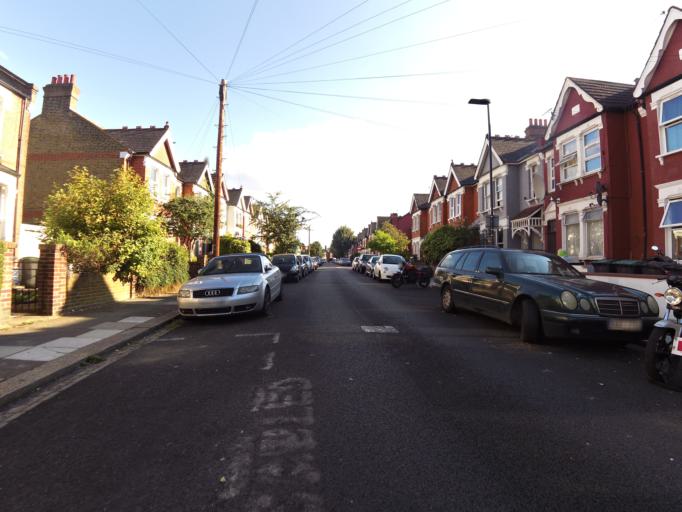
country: GB
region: England
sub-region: Greater London
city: Harringay
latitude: 51.5962
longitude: -0.0757
